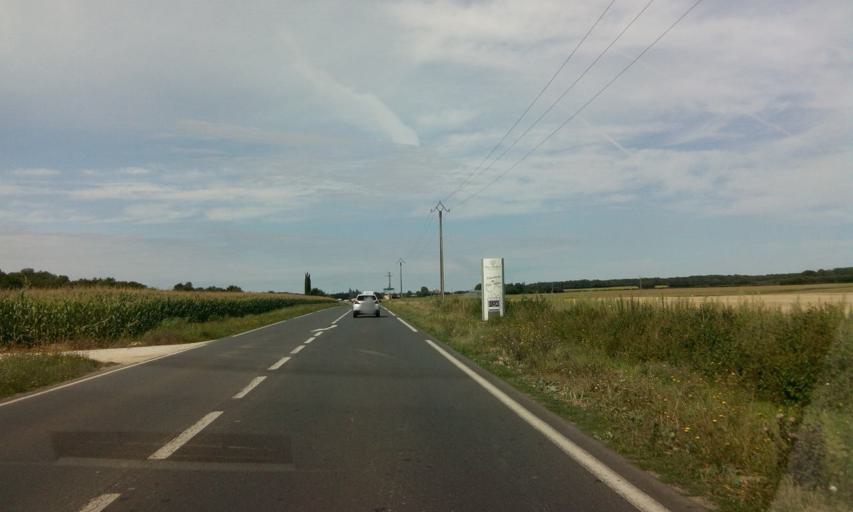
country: FR
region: Poitou-Charentes
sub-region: Departement des Deux-Sevres
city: Sauze-Vaussais
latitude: 46.1372
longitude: 0.1700
